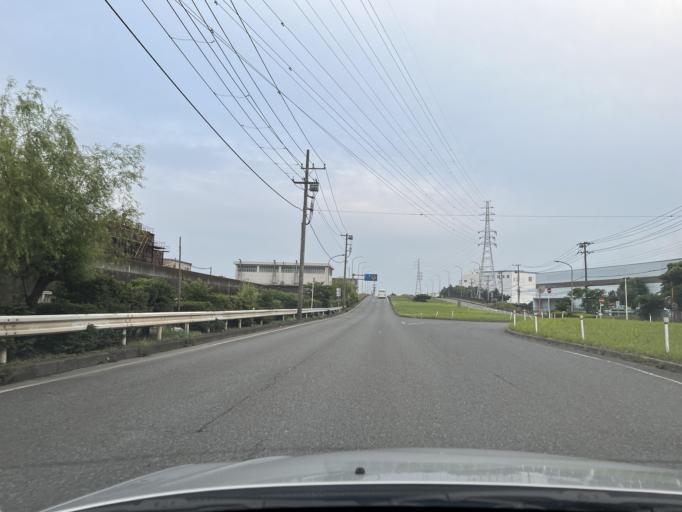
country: JP
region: Chiba
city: Funabashi
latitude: 35.6835
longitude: 139.9628
